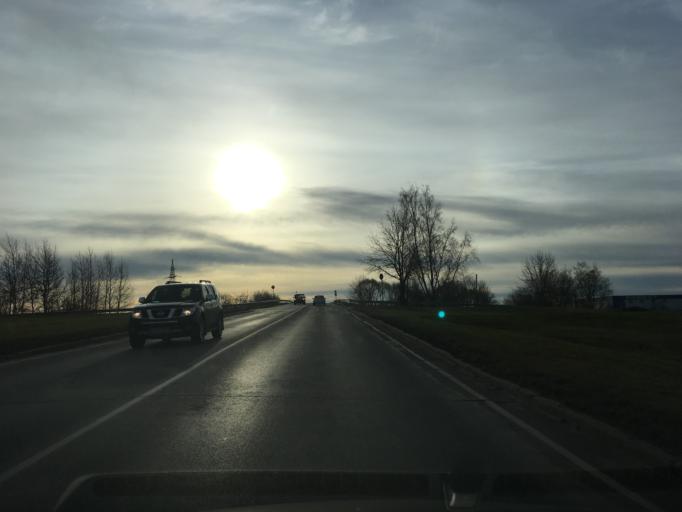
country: EE
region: Ida-Virumaa
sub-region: Narva linn
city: Narva
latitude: 59.3738
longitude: 28.1547
